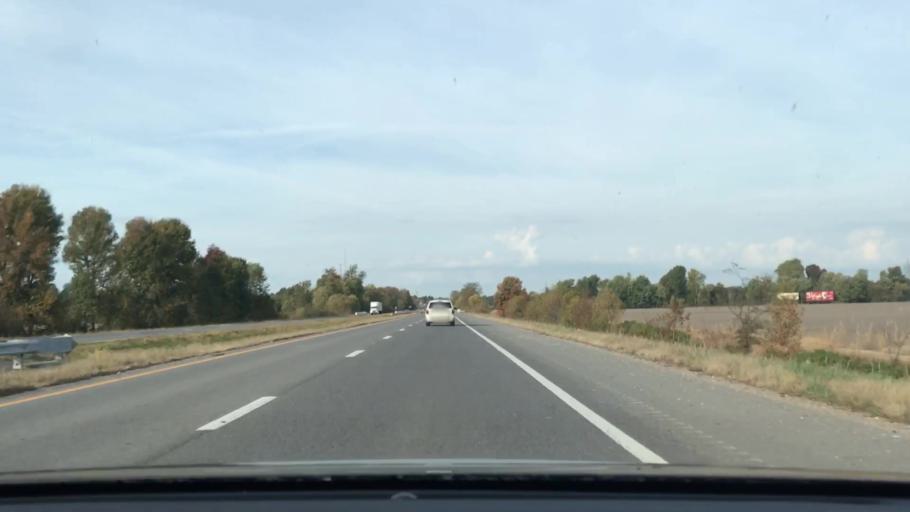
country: US
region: Kentucky
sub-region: Graves County
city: Mayfield
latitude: 36.7695
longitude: -88.6243
